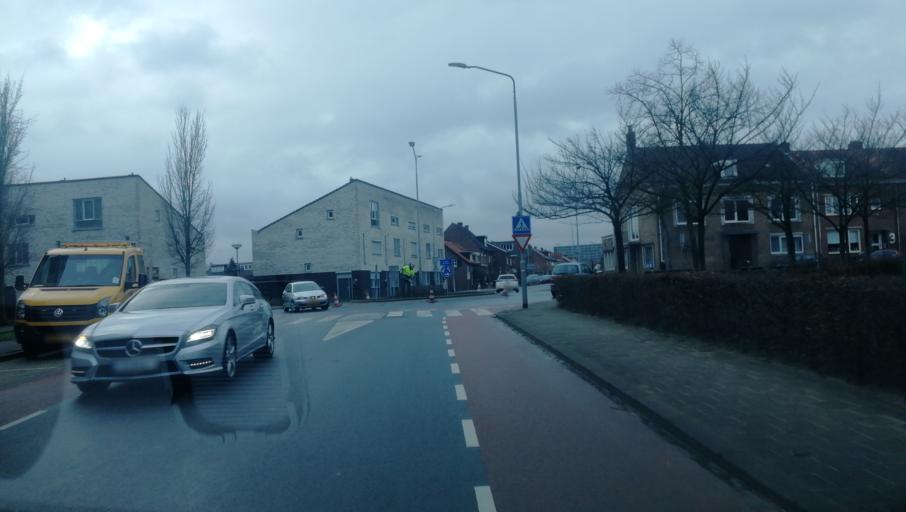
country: NL
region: Limburg
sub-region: Gemeente Venlo
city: Venlo
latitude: 51.3676
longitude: 6.1479
